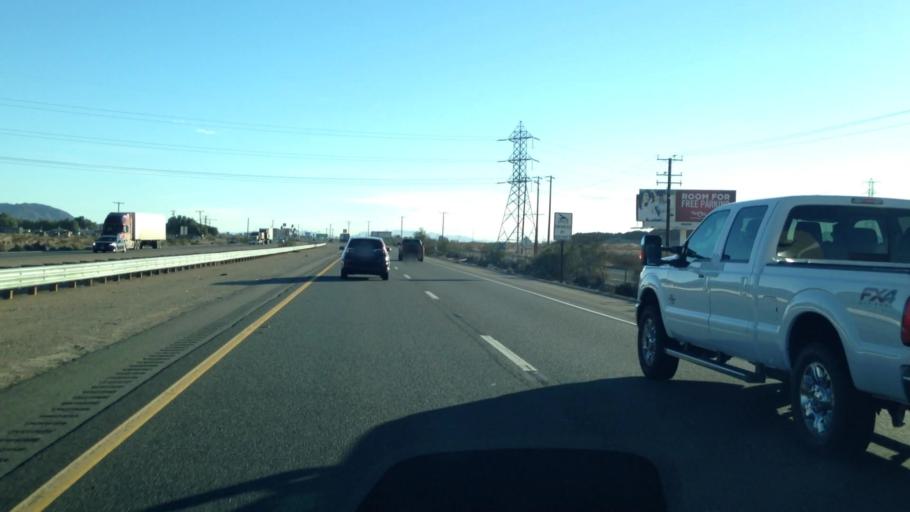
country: US
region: California
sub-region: San Bernardino County
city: Barstow
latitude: 34.9011
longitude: -116.9020
